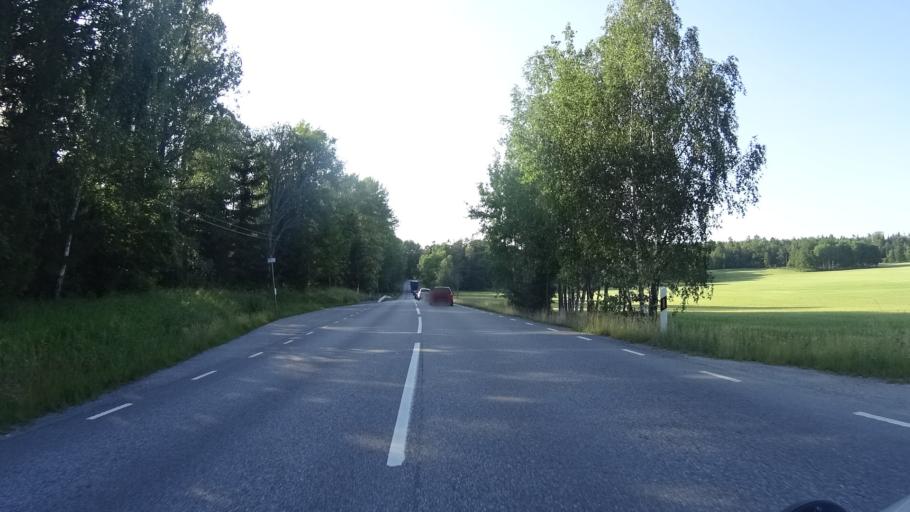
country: SE
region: Stockholm
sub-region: Sodertalje Kommun
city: Pershagen
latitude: 59.1129
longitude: 17.6426
